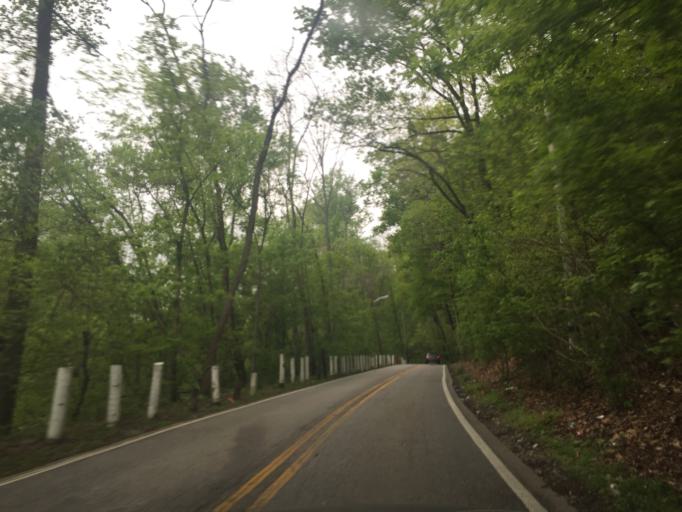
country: US
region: Maryland
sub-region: Baltimore County
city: Charlestown
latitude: 39.3034
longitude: -76.6747
